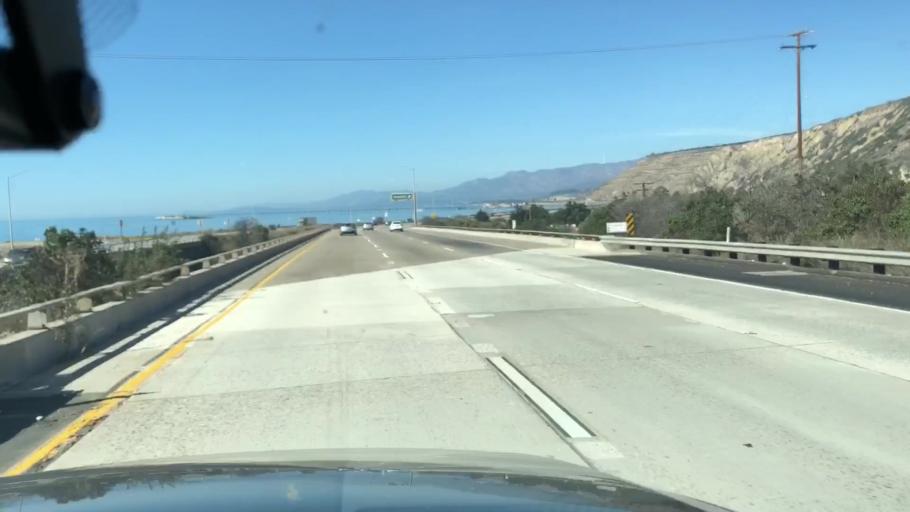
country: US
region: California
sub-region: Santa Barbara County
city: Carpinteria
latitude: 34.3431
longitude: -119.4158
